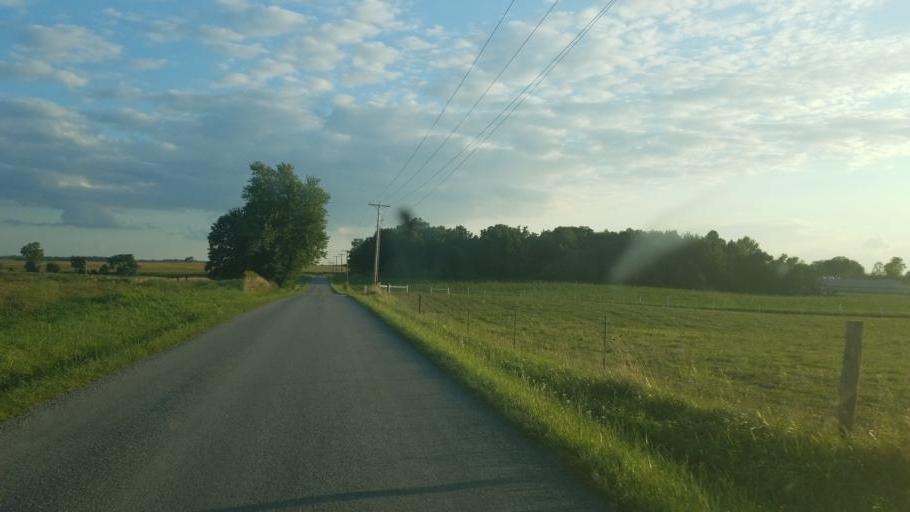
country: US
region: Ohio
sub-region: Huron County
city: Greenwich
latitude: 40.9797
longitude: -82.5584
